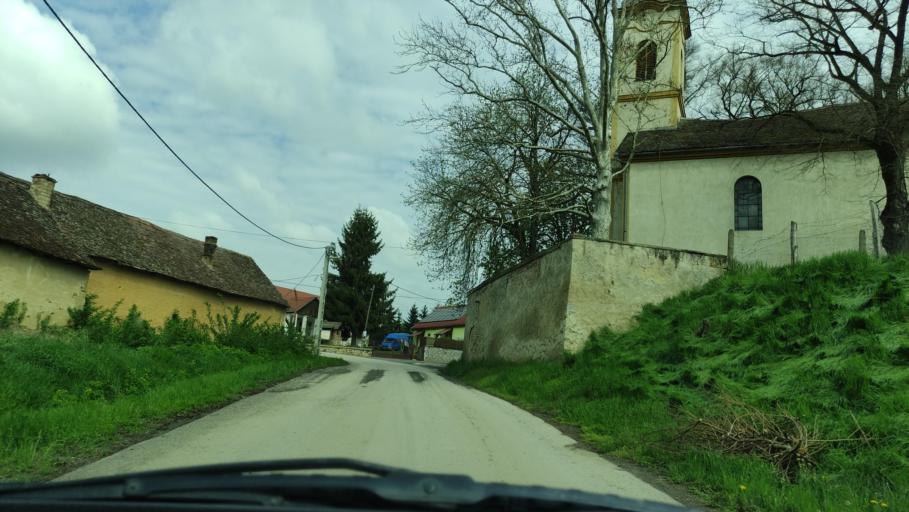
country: HU
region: Baranya
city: Magocs
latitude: 46.2739
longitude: 18.2152
